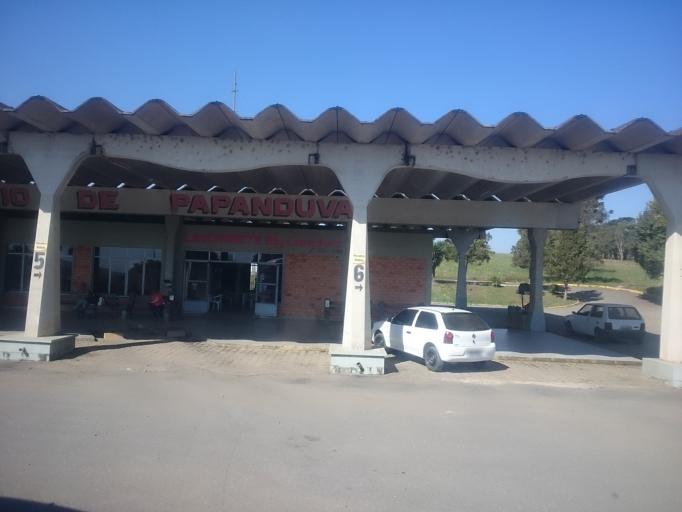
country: BR
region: Santa Catarina
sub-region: Canoinhas
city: Canoinhas
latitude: -26.4103
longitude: -50.1468
